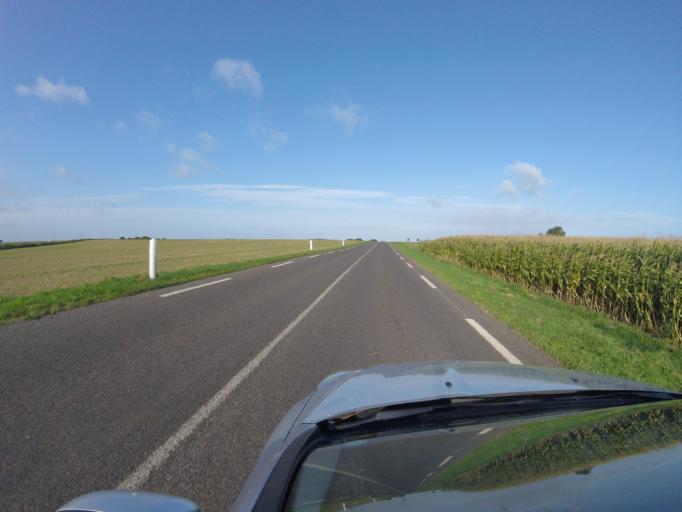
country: FR
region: Haute-Normandie
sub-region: Departement de la Seine-Maritime
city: Fecamp
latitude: 49.7671
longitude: 0.4146
